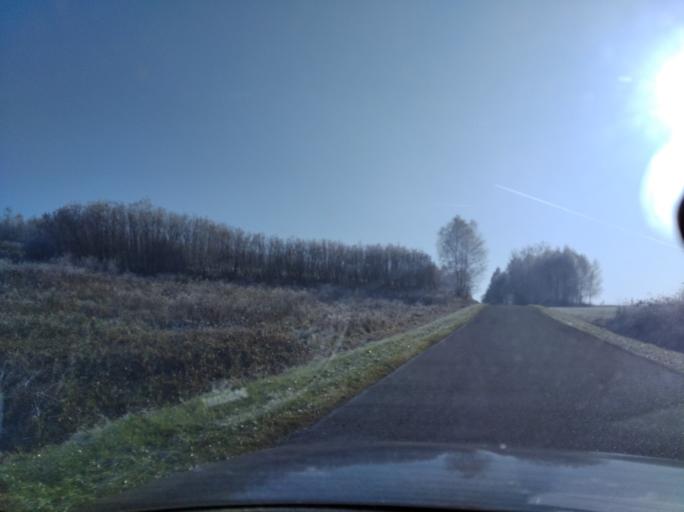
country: PL
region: Subcarpathian Voivodeship
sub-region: Powiat strzyzowski
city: Wysoka Strzyzowska
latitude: 49.8397
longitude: 21.7098
